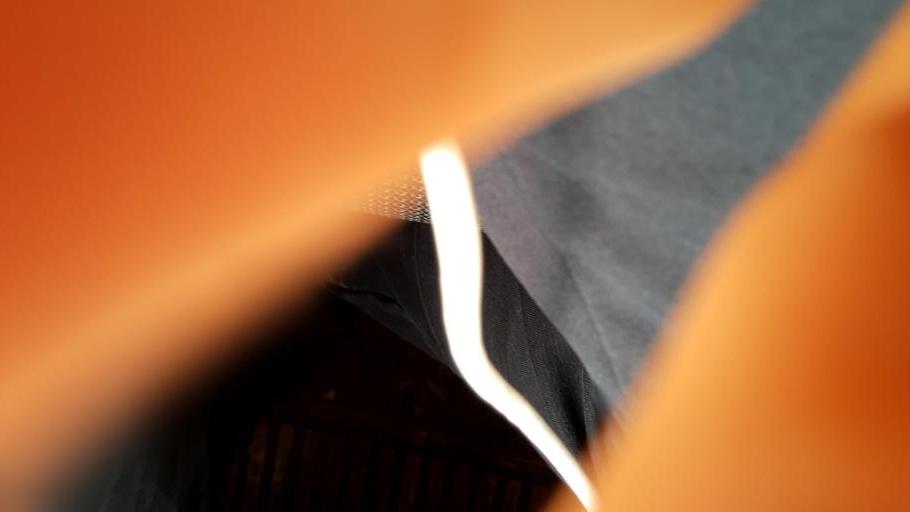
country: RU
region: Bashkortostan
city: Pavlovka
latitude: 55.3785
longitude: 56.4230
